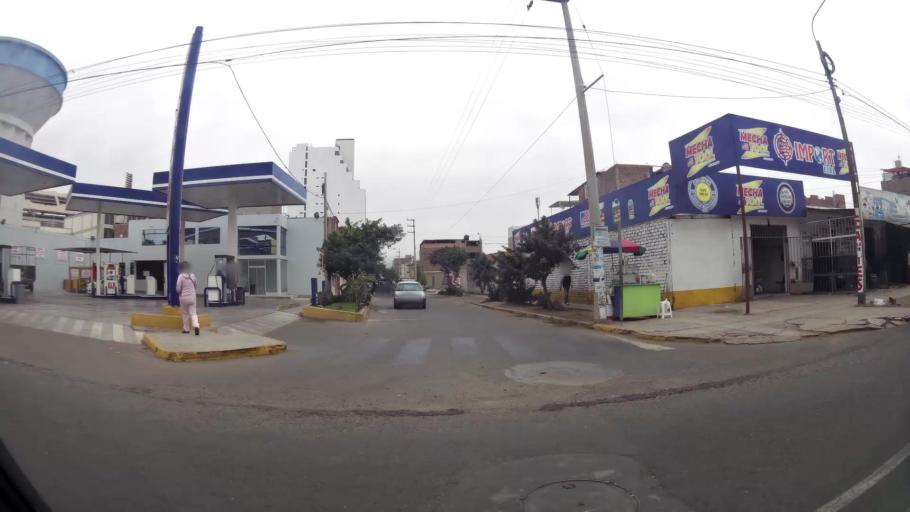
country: PE
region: La Libertad
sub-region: Provincia de Trujillo
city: Trujillo
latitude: -8.1188
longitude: -79.0183
